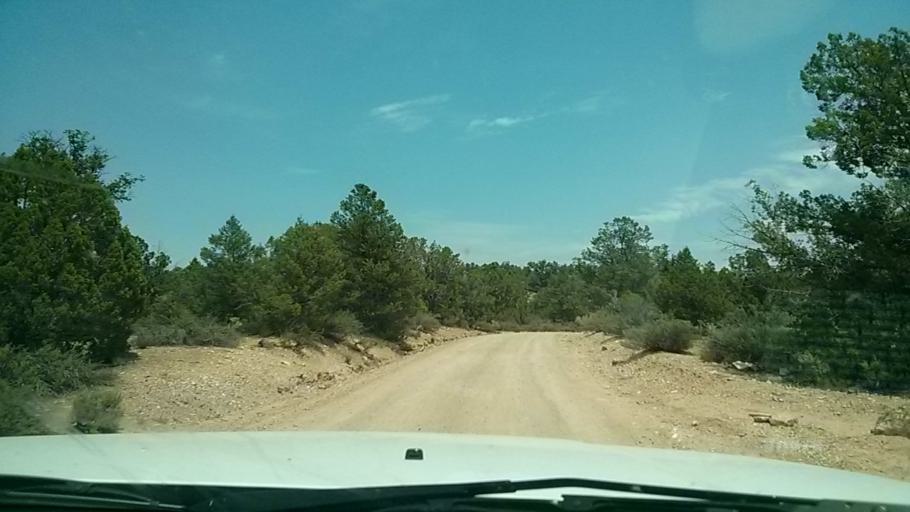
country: US
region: Utah
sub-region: Washington County
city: Washington
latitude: 37.2366
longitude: -113.4539
